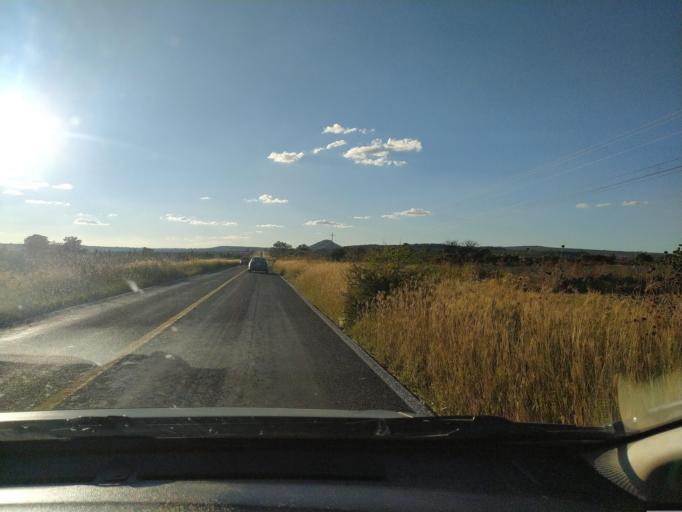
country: MX
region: Jalisco
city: San Diego de Alejandria
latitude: 21.0056
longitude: -102.0587
